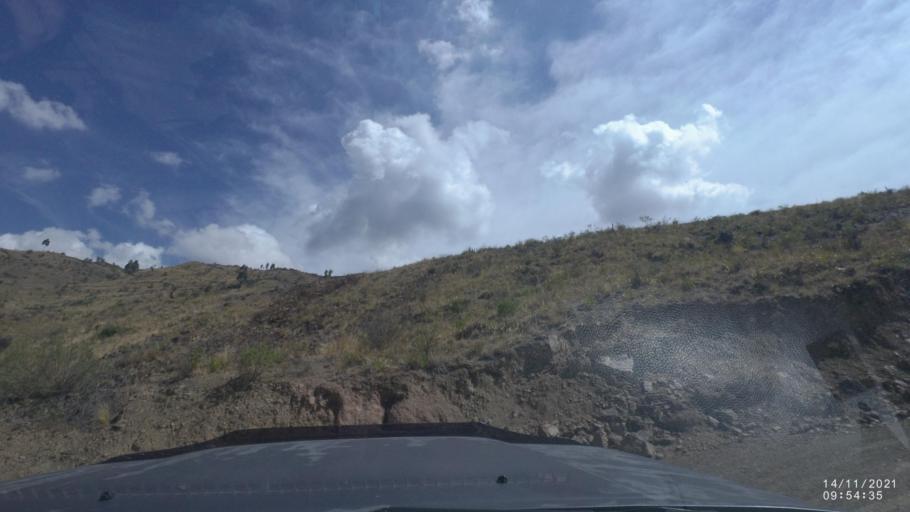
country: BO
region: Cochabamba
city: Cochabamba
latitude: -17.3583
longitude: -66.0884
